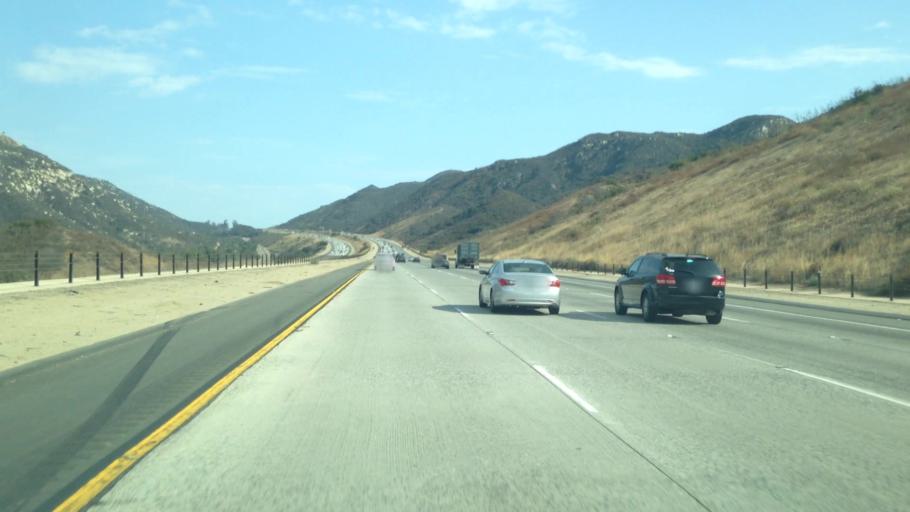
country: US
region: California
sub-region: San Diego County
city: Hidden Meadows
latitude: 33.2281
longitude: -117.1450
